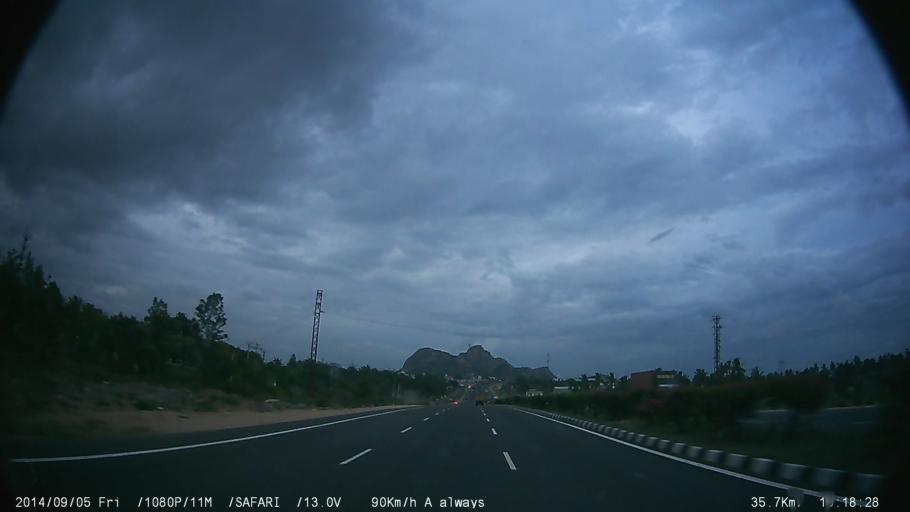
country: IN
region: Tamil Nadu
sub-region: Krishnagiri
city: Kelamangalam
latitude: 12.6673
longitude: 77.9949
